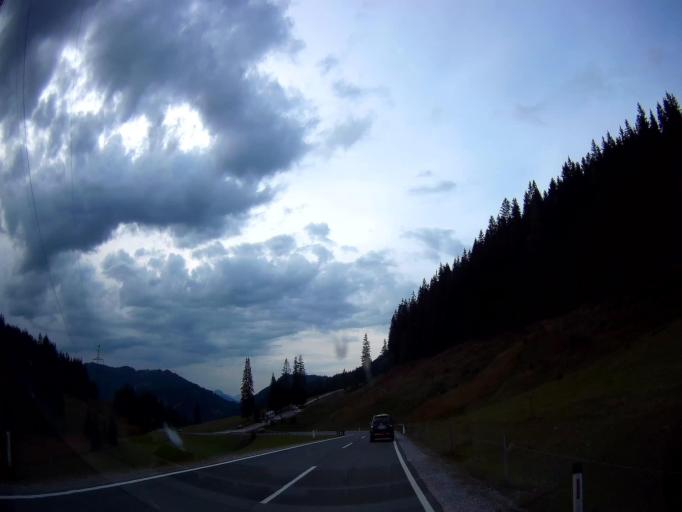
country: AT
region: Salzburg
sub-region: Politischer Bezirk Zell am See
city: Dienten am Hochkonig
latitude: 47.3913
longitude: 13.0516
